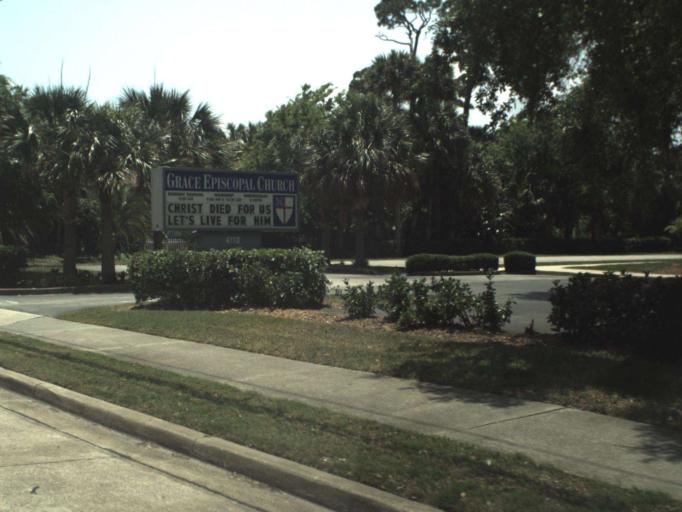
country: US
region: Florida
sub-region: Volusia County
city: Port Orange
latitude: 29.1419
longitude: -80.9867
